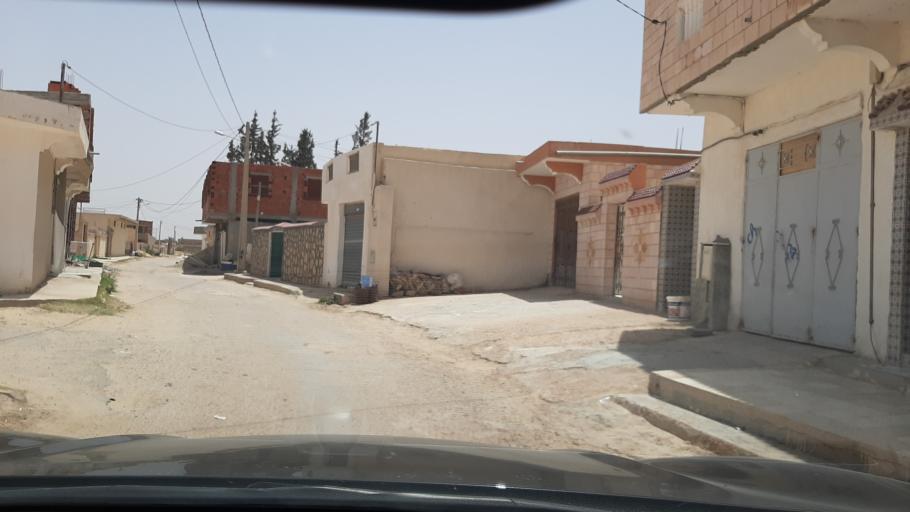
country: TN
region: Qabis
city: Matmata
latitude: 33.6167
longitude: 10.2768
